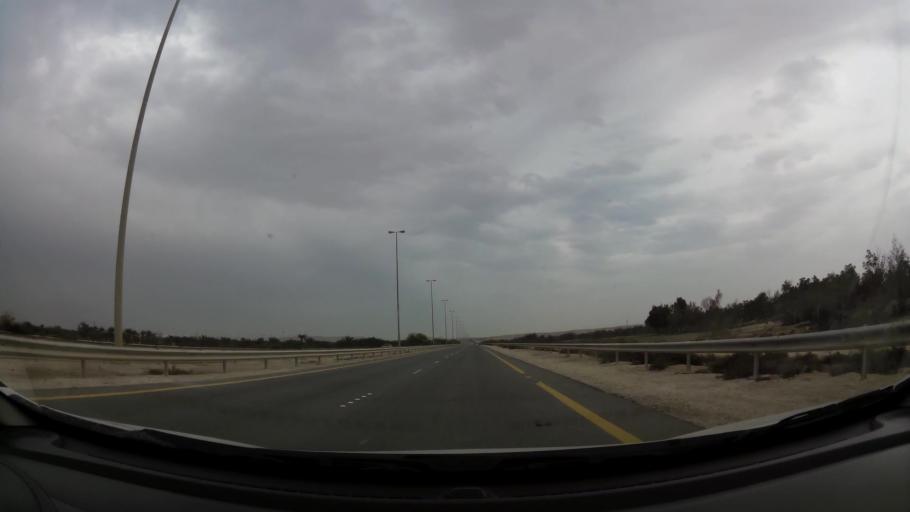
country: BH
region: Central Governorate
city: Dar Kulayb
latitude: 26.0192
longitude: 50.4960
